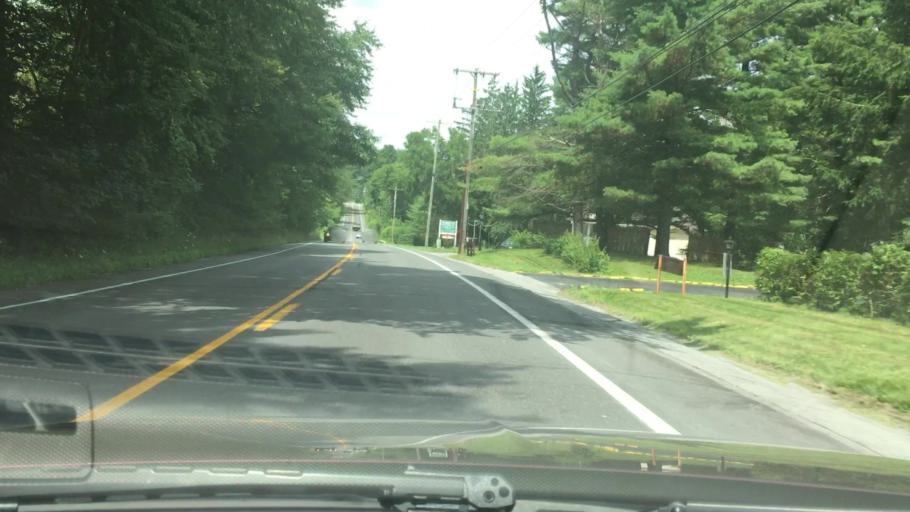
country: US
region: New York
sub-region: Dutchess County
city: Pawling
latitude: 41.6201
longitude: -73.6793
